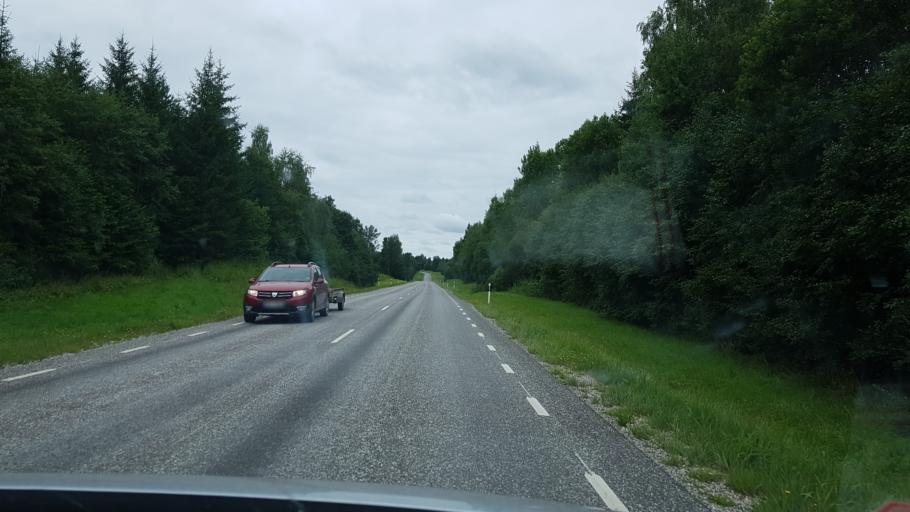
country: EE
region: Vorumaa
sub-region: Antsla vald
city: Vana-Antsla
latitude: 58.0048
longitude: 26.6982
